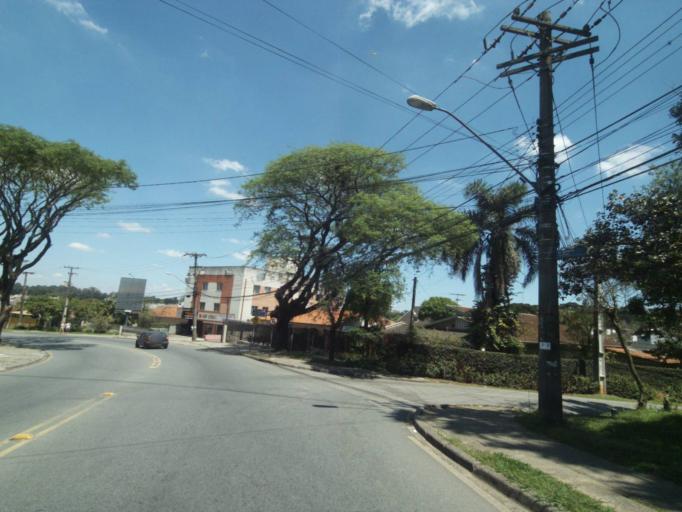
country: BR
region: Parana
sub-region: Curitiba
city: Curitiba
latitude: -25.3882
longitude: -49.2230
